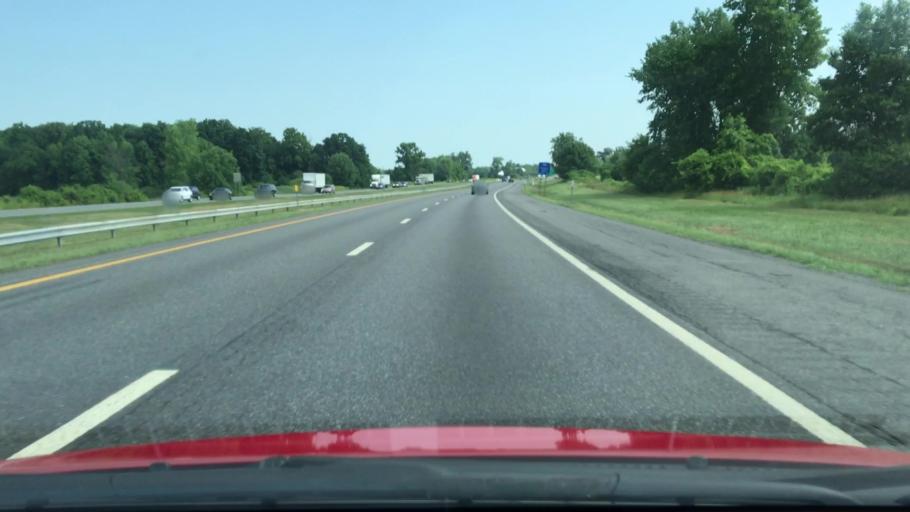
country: US
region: New York
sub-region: Rensselaer County
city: Castleton-on-Hudson
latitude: 42.5691
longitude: -73.7895
